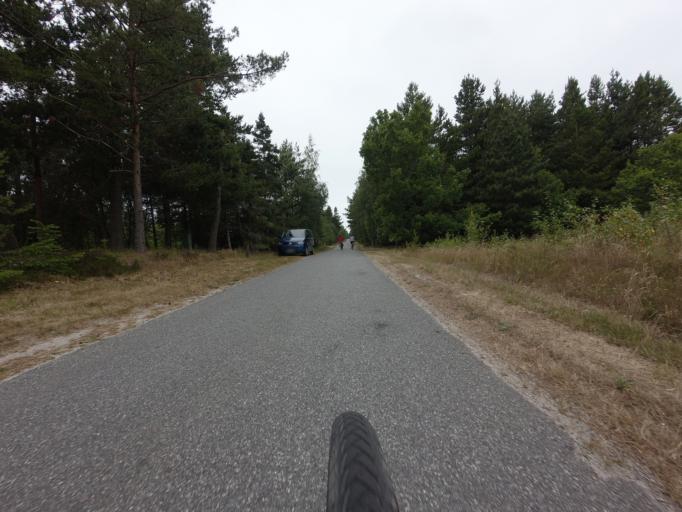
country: DK
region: North Denmark
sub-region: Laeso Kommune
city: Byrum
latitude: 57.2775
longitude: 10.9614
